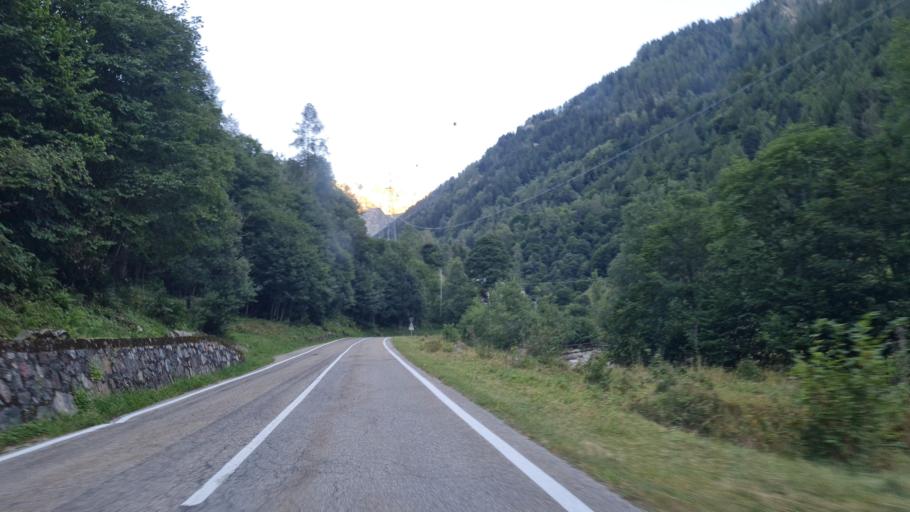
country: IT
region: Piedmont
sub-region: Provincia di Vercelli
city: Rima
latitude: 45.8750
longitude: 8.0164
